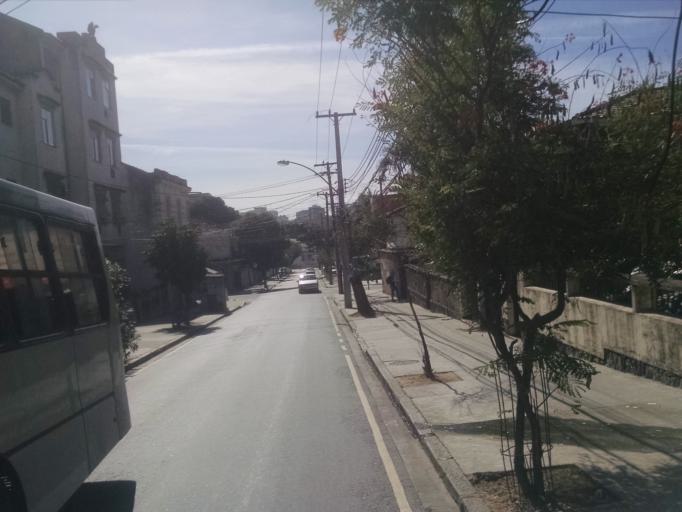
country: BR
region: Rio de Janeiro
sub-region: Rio De Janeiro
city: Rio de Janeiro
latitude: -22.9129
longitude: -43.2700
